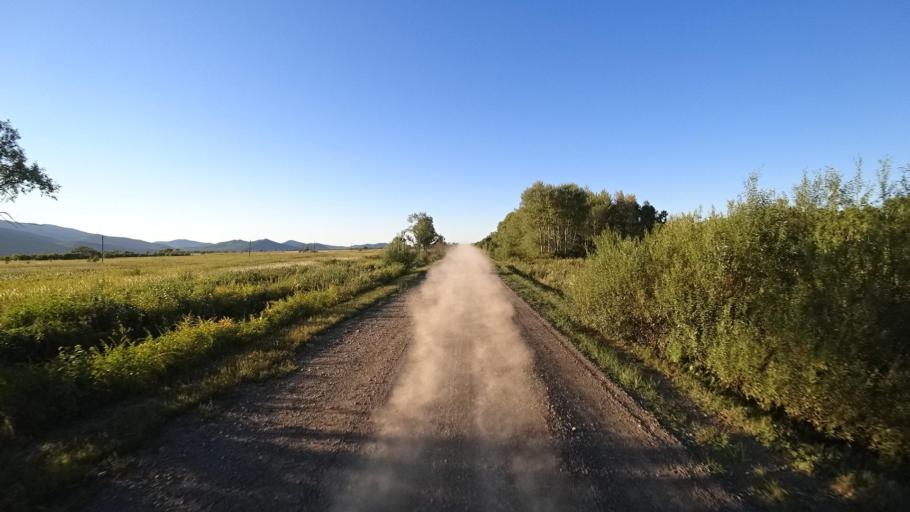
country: RU
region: Primorskiy
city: Kirovskiy
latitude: 44.7913
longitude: 133.6228
